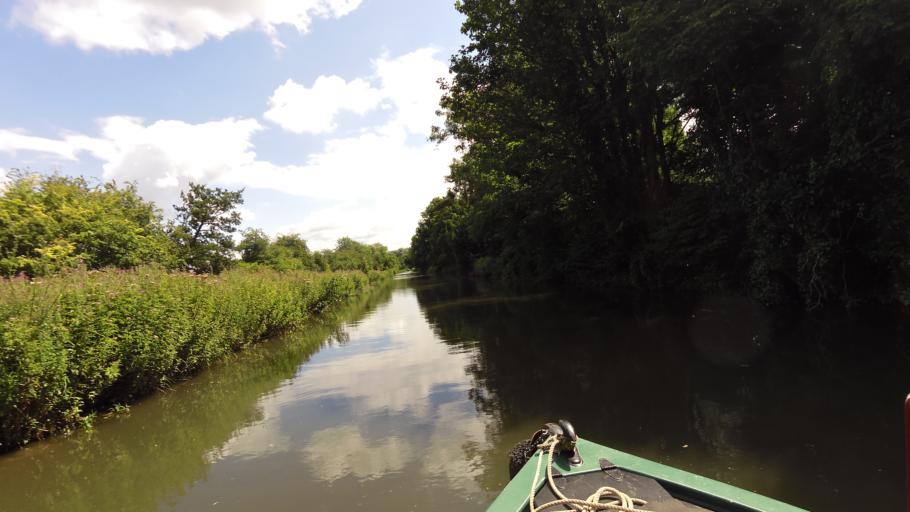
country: GB
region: England
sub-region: West Berkshire
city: Kintbury
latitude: 51.3997
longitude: -1.3873
